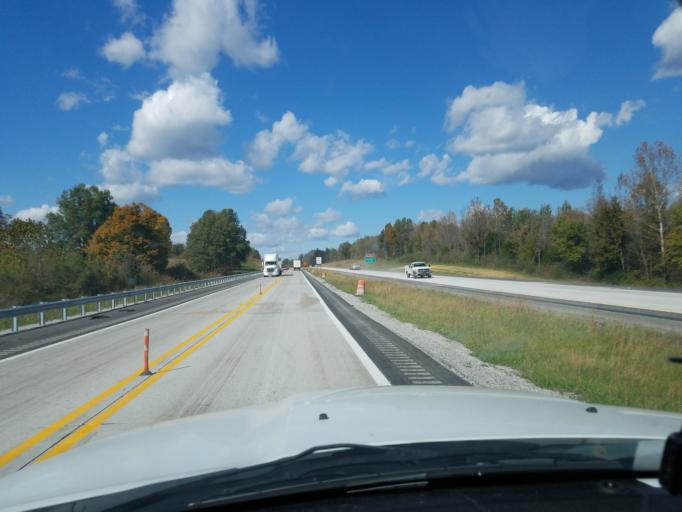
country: US
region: Kentucky
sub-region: Ohio County
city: Beaver Dam
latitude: 37.4397
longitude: -86.8572
